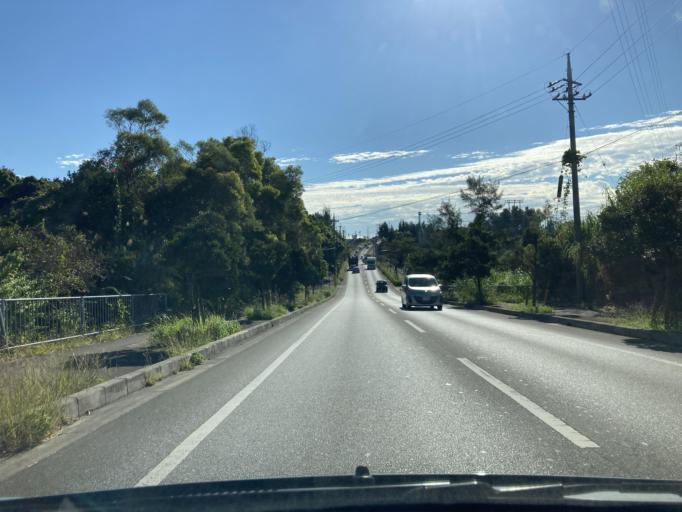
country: JP
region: Okinawa
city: Okinawa
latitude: 26.3718
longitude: 127.7683
